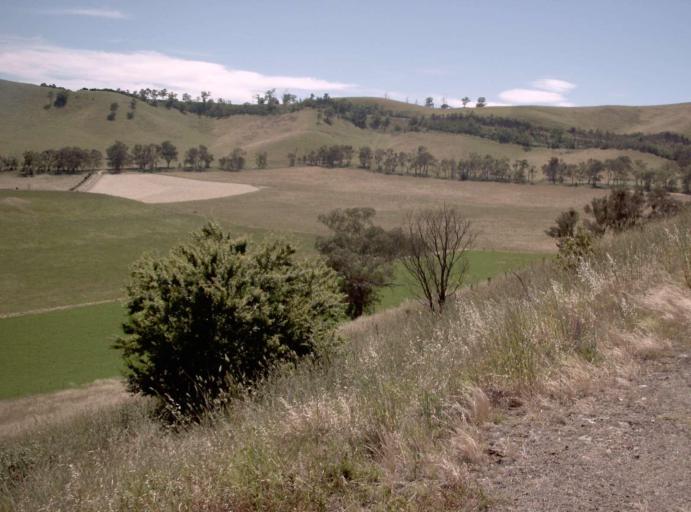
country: AU
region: Victoria
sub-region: East Gippsland
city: Lakes Entrance
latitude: -37.4903
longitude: 148.1742
